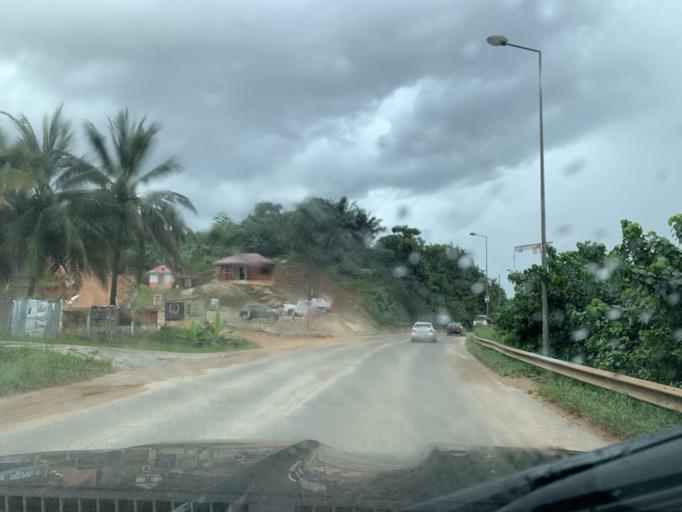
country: GH
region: Western
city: Tarkwa
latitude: 5.3186
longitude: -1.9875
